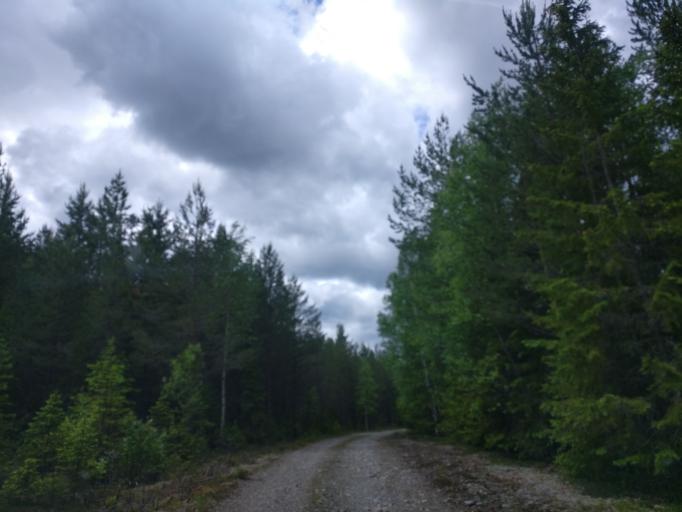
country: SE
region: Jaemtland
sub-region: Harjedalens Kommun
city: Sveg
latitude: 62.1952
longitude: 13.4155
